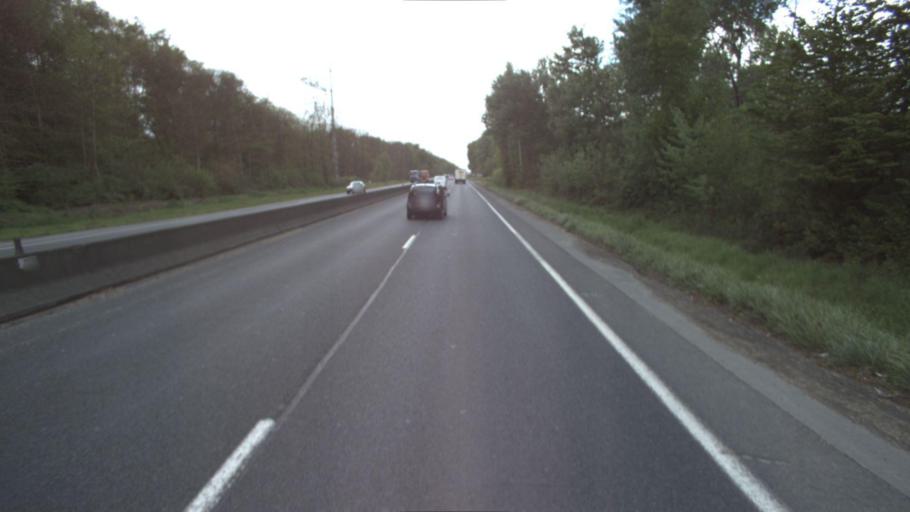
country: FR
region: Ile-de-France
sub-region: Departement de Seine-et-Marne
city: Roissy-en-Brie
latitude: 48.7698
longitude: 2.6355
